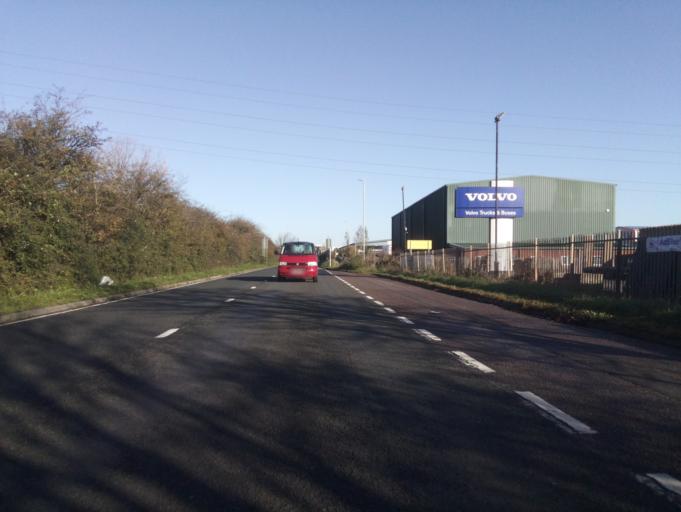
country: GB
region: England
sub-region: Somerset
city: Puriton
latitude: 51.1522
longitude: -2.9884
